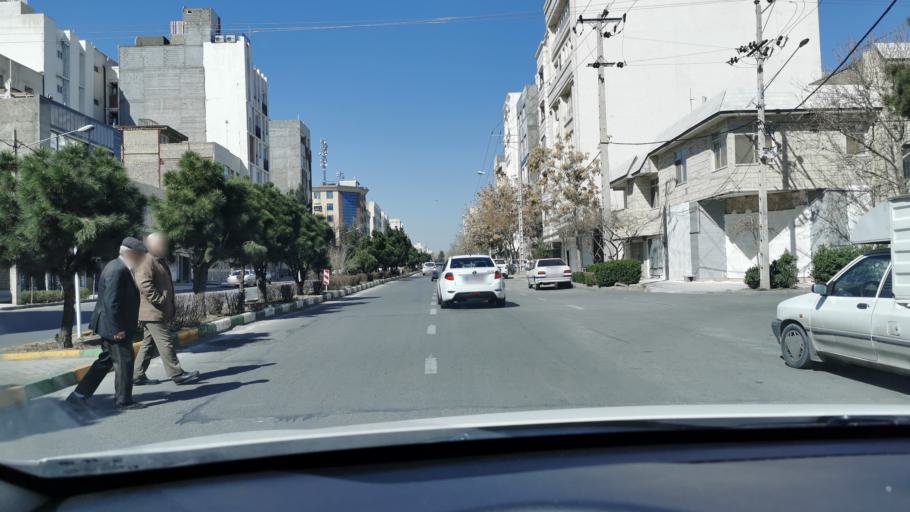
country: IR
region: Razavi Khorasan
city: Mashhad
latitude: 36.3249
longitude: 59.5252
